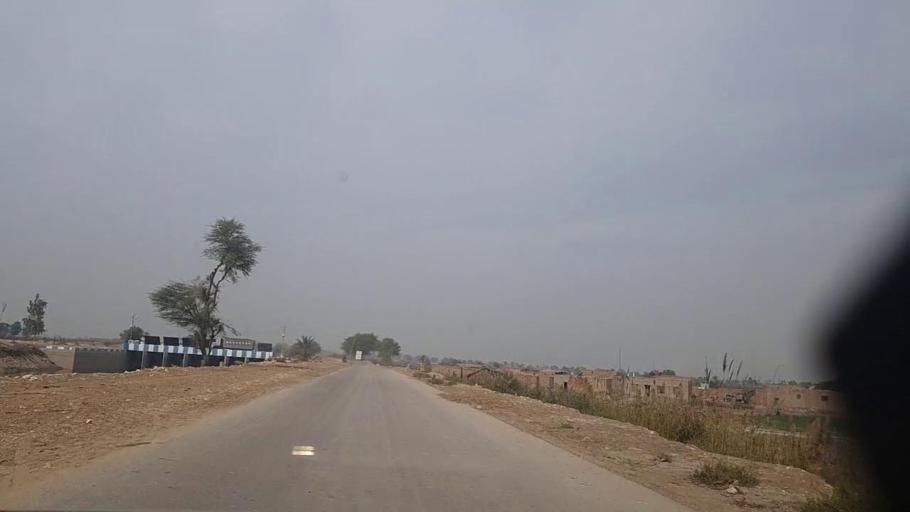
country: PK
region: Sindh
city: Sakrand
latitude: 26.2832
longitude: 68.2266
